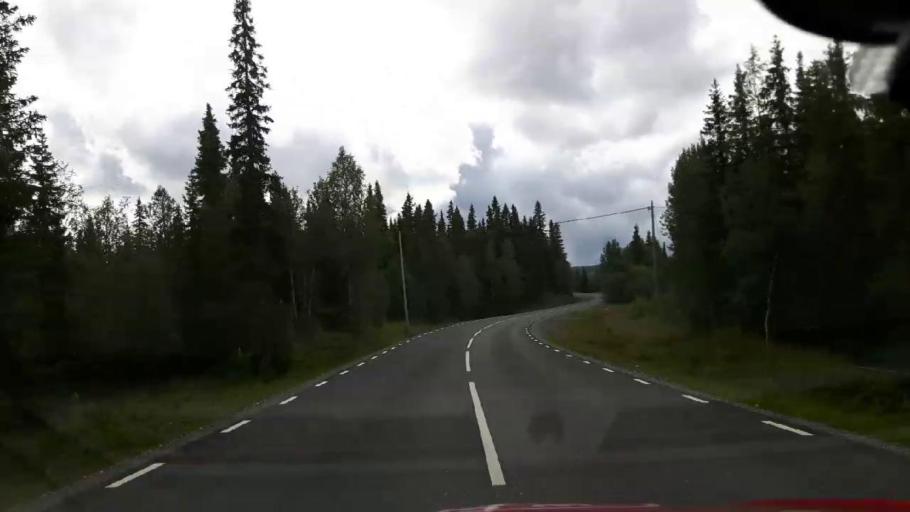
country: NO
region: Nord-Trondelag
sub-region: Lierne
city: Sandvika
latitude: 64.5934
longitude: 14.1154
